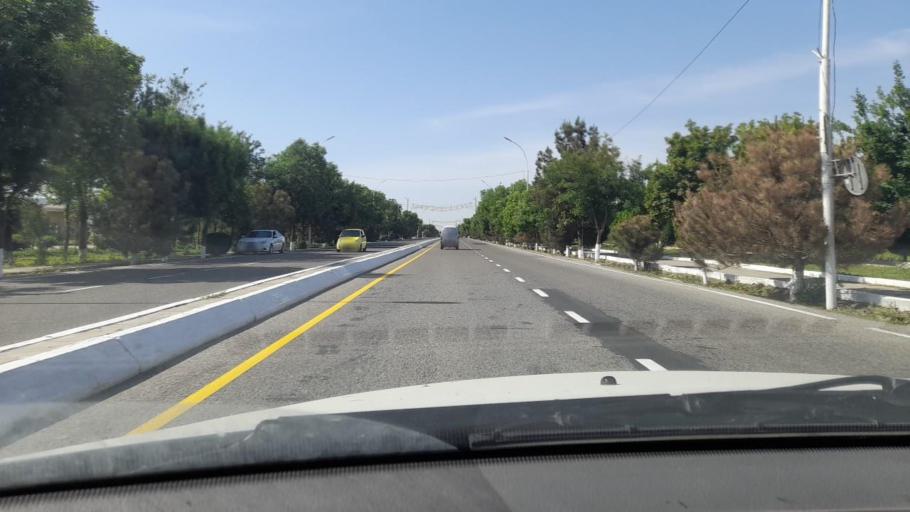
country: UZ
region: Bukhara
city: Bukhara
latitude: 39.7967
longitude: 64.4351
